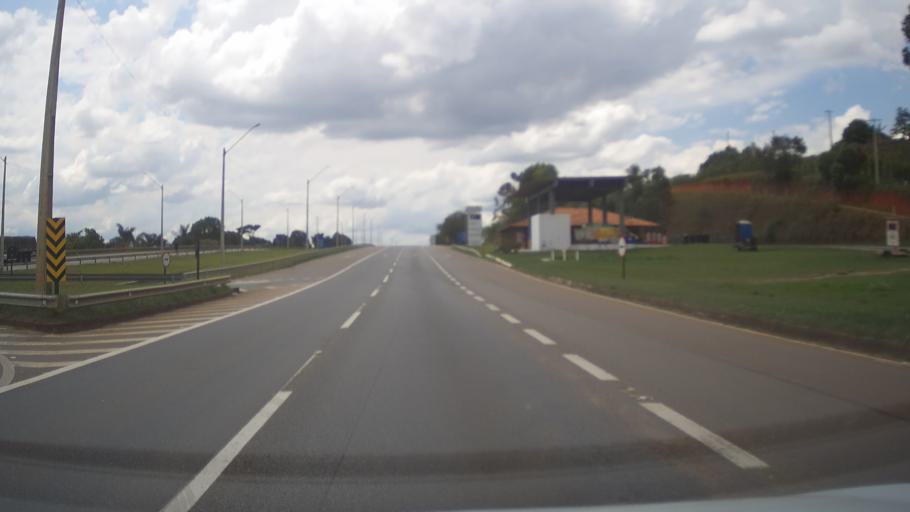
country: BR
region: Minas Gerais
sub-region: Nepomuceno
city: Nepomuceno
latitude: -21.2670
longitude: -45.1375
